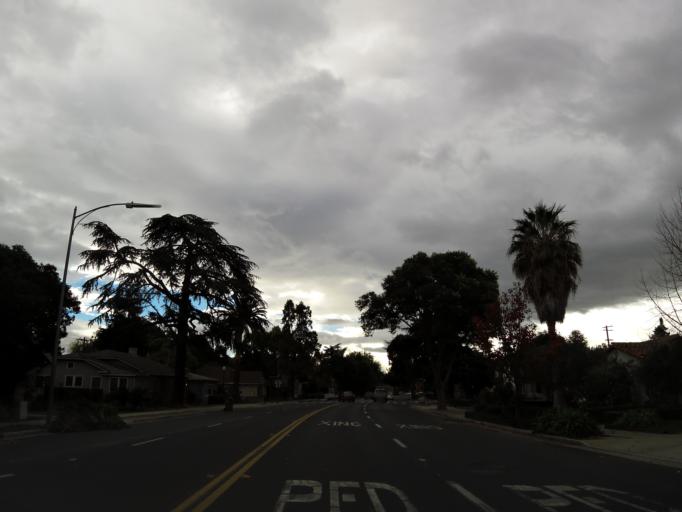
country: US
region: California
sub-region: Santa Clara County
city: Buena Vista
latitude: 37.3012
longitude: -121.8947
